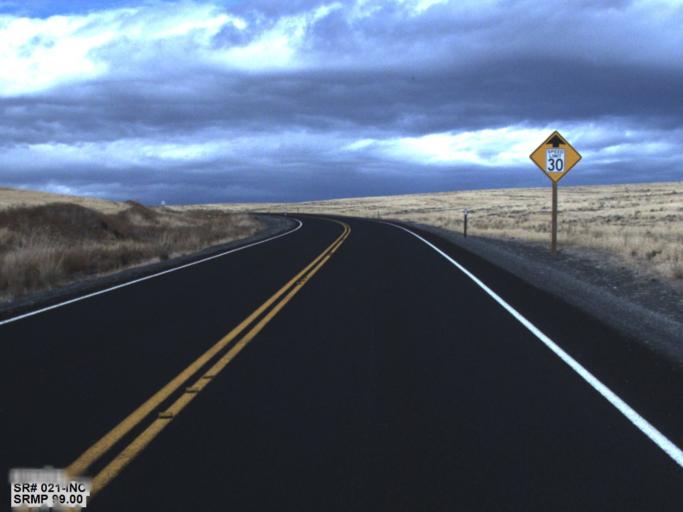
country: US
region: Washington
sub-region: Okanogan County
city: Coulee Dam
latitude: 47.8568
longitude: -118.7184
